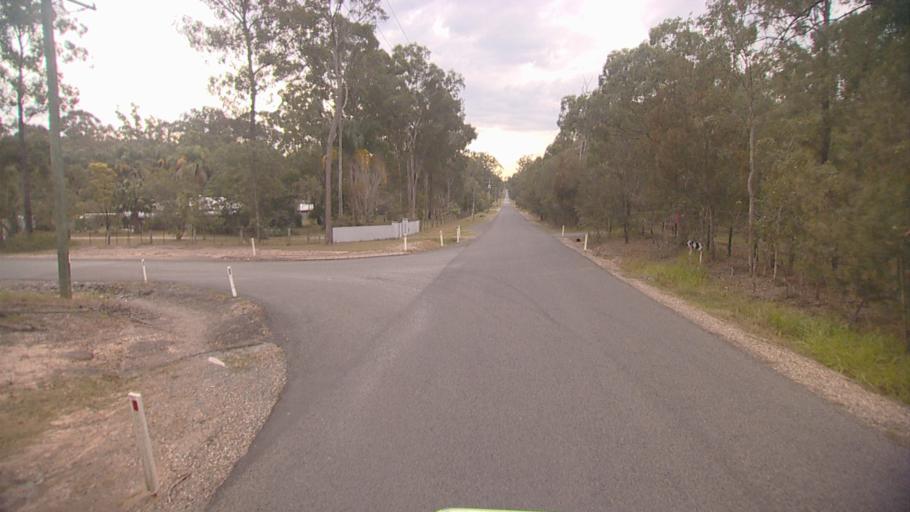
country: AU
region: Queensland
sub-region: Logan
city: Chambers Flat
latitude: -27.7944
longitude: 153.1217
